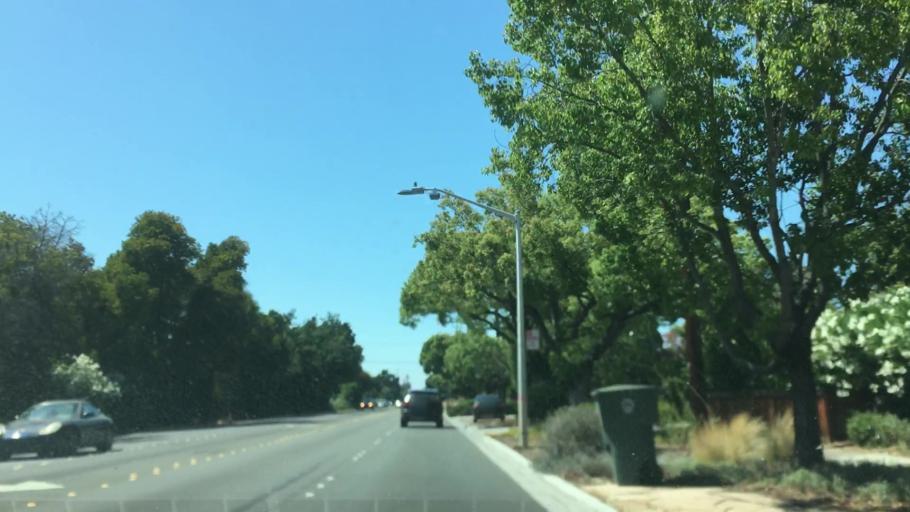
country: US
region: California
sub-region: Santa Clara County
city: Palo Alto
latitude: 37.4220
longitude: -122.1298
